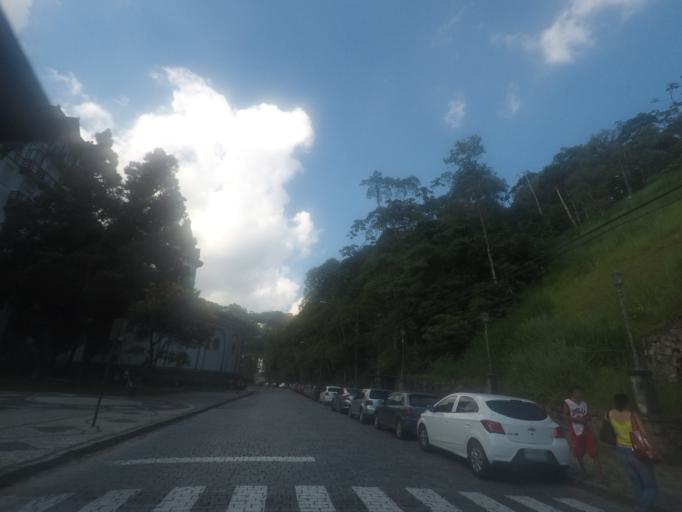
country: BR
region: Rio de Janeiro
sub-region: Petropolis
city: Petropolis
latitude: -22.5275
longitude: -43.2118
